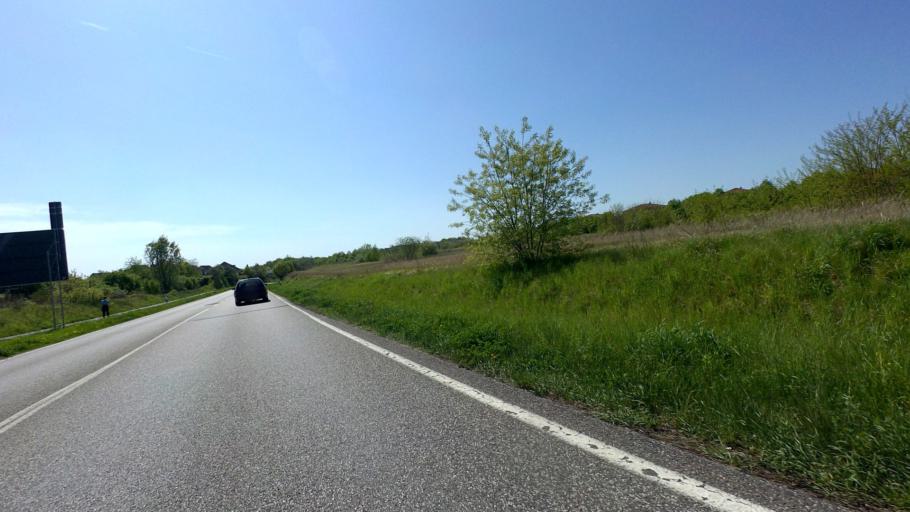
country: DE
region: Brandenburg
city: Konigs Wusterhausen
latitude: 52.3012
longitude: 13.6023
